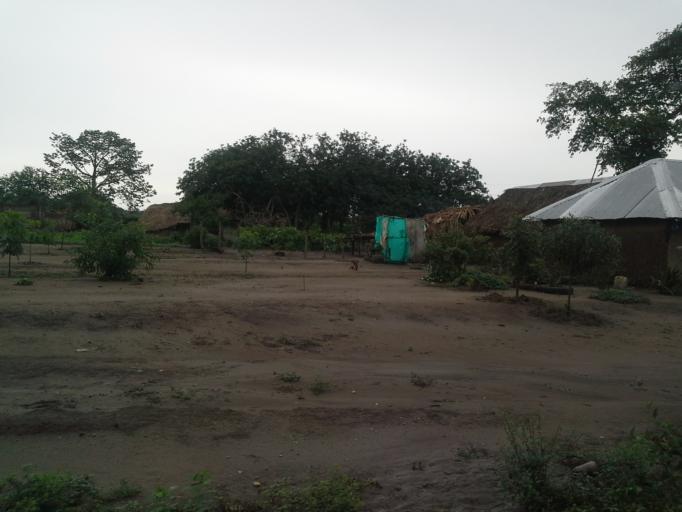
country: CO
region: Sucre
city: Coloso
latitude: 9.4566
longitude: -75.3279
